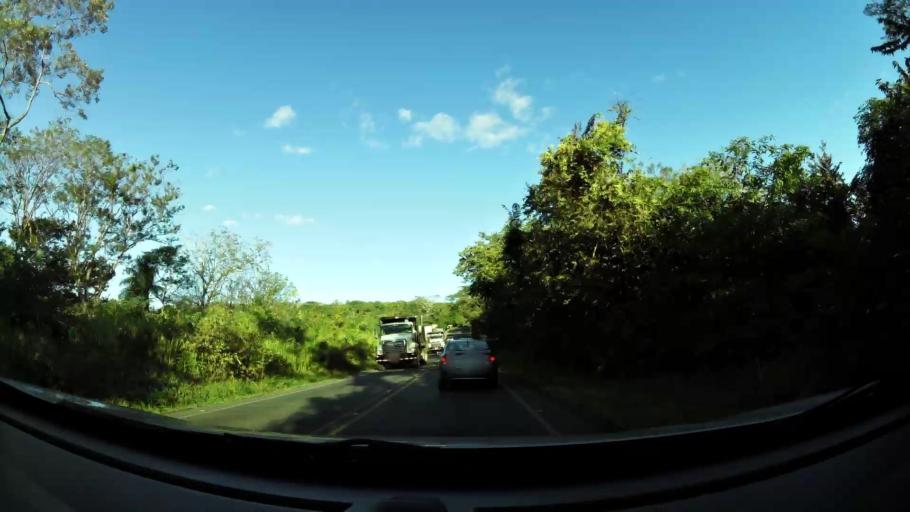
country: CR
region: Puntarenas
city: Miramar
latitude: 10.0898
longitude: -84.7946
